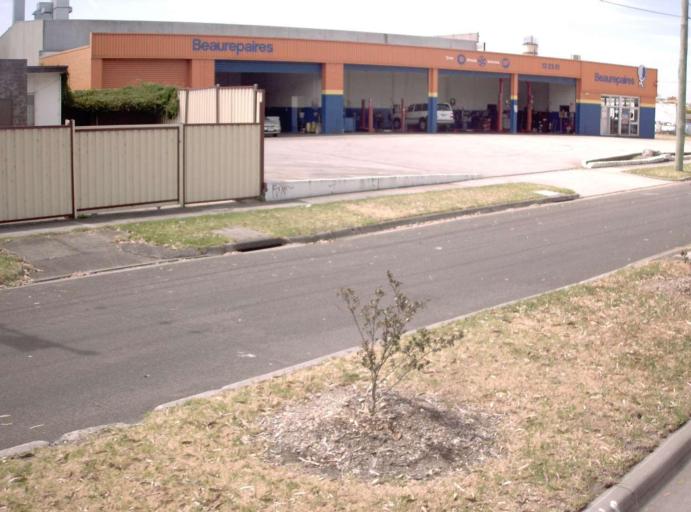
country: AU
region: Victoria
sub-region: Greater Dandenong
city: Keysborough
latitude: -37.9935
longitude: 145.1875
